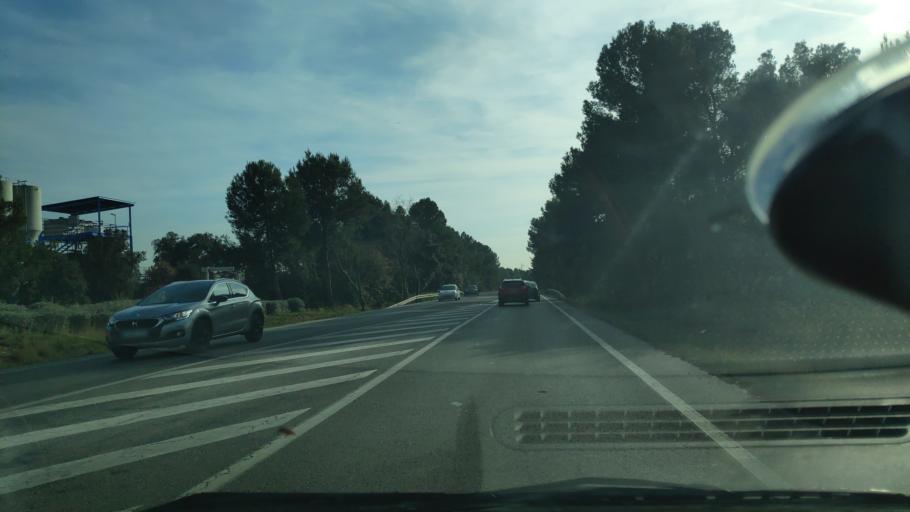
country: ES
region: Catalonia
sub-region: Provincia de Barcelona
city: Castellar del Valles
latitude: 41.5886
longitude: 2.0895
